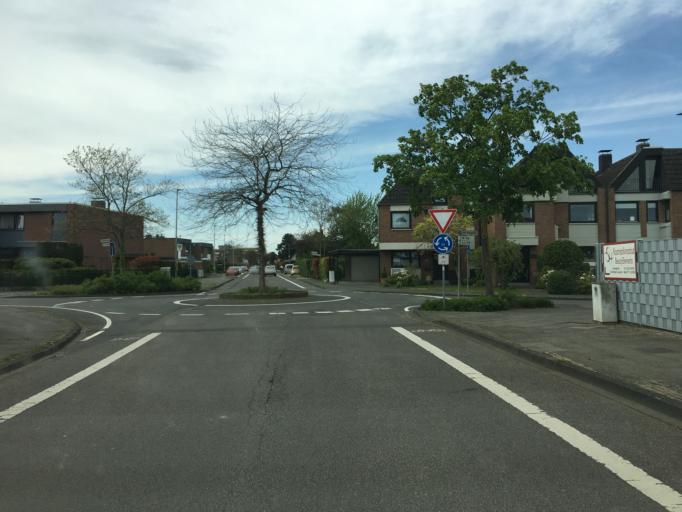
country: DE
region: North Rhine-Westphalia
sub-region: Regierungsbezirk Koln
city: Erftstadt
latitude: 50.8059
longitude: 6.7795
